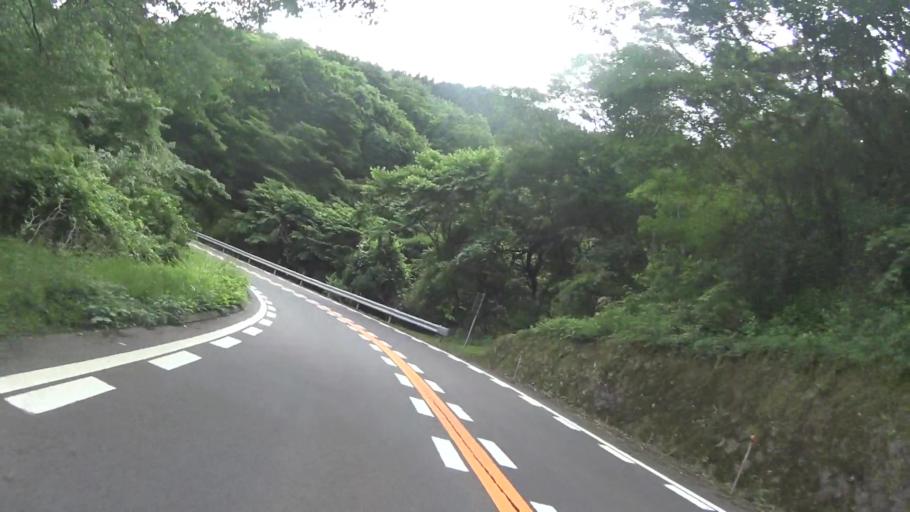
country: JP
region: Oita
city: Tsukawaki
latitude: 33.2316
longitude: 131.2938
